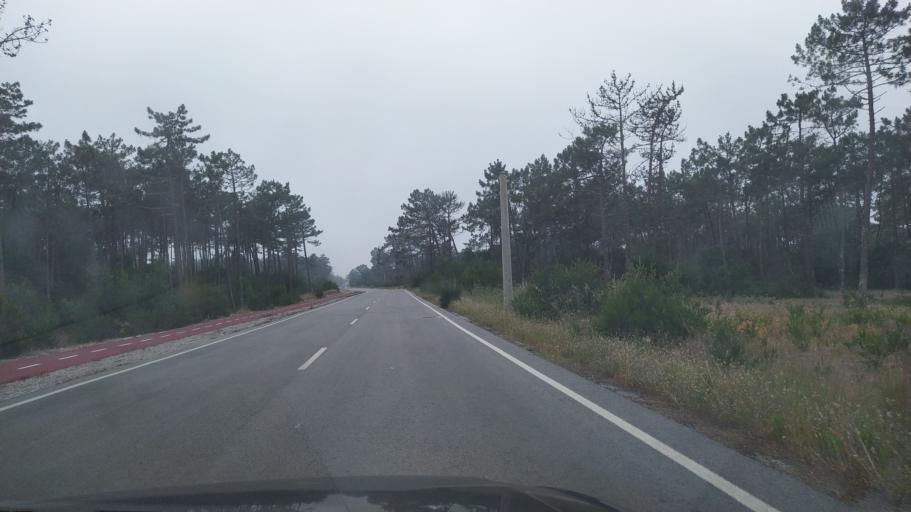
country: PT
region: Aveiro
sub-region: Ilhavo
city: Gafanha da Encarnacao
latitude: 40.5699
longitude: -8.7378
